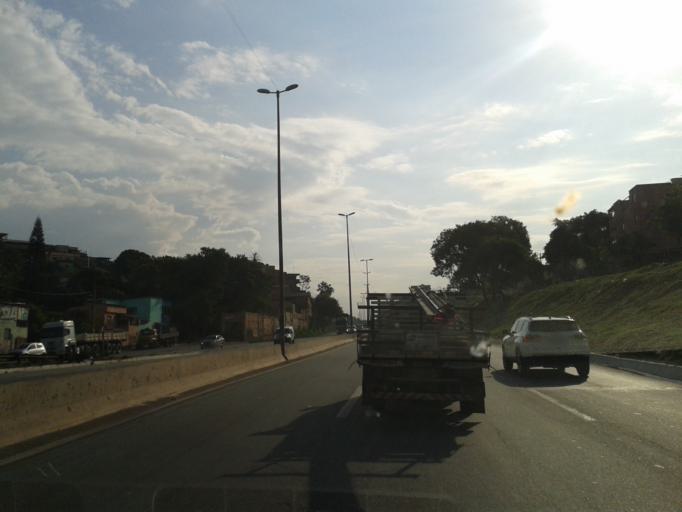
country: BR
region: Minas Gerais
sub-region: Belo Horizonte
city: Belo Horizonte
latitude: -19.8670
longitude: -43.9330
